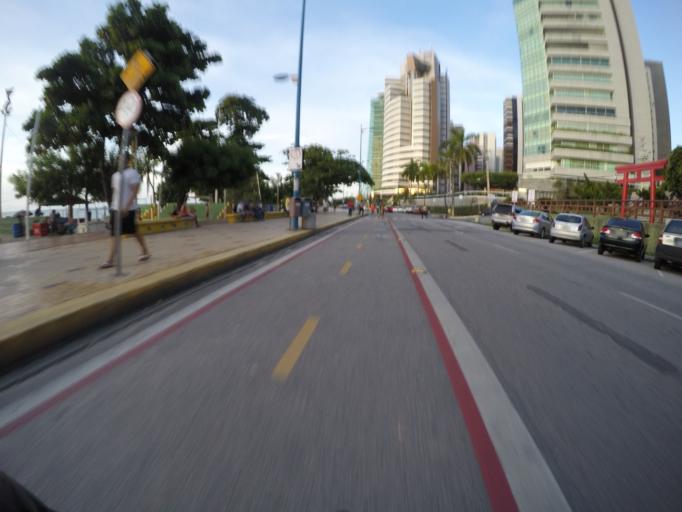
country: BR
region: Ceara
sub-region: Fortaleza
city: Fortaleza
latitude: -3.7251
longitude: -38.4910
